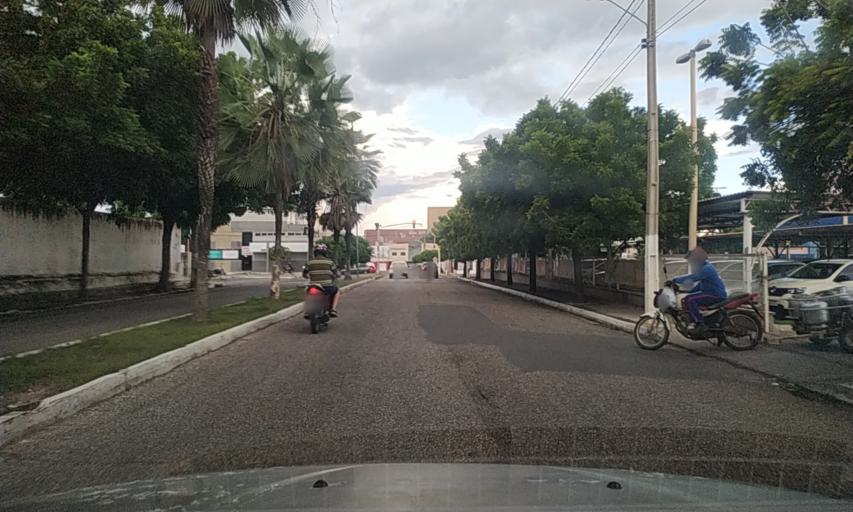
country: BR
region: Rio Grande do Norte
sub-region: Mossoro
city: Mossoro
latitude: -5.1898
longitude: -37.3477
